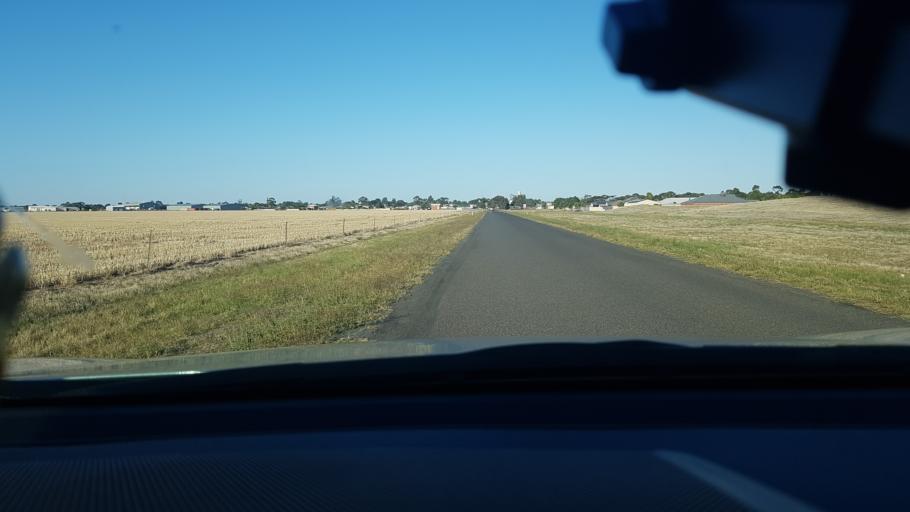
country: AU
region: Victoria
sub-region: Horsham
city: Horsham
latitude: -36.7123
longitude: 142.1754
